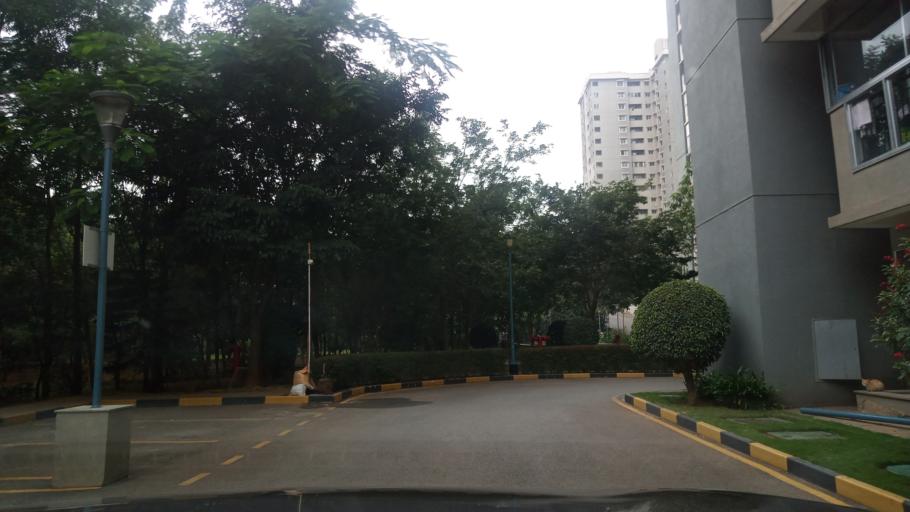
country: IN
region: Karnataka
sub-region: Bangalore Urban
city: Yelahanka
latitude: 13.0453
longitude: 77.4999
